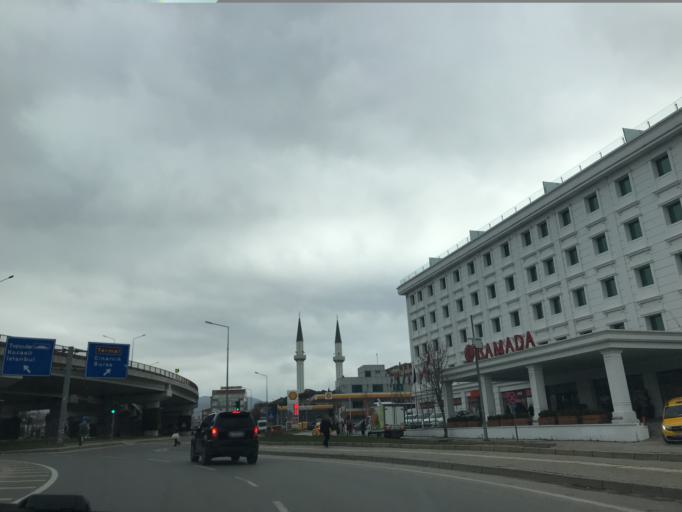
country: TR
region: Yalova
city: Yalova
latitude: 40.6565
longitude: 29.2833
